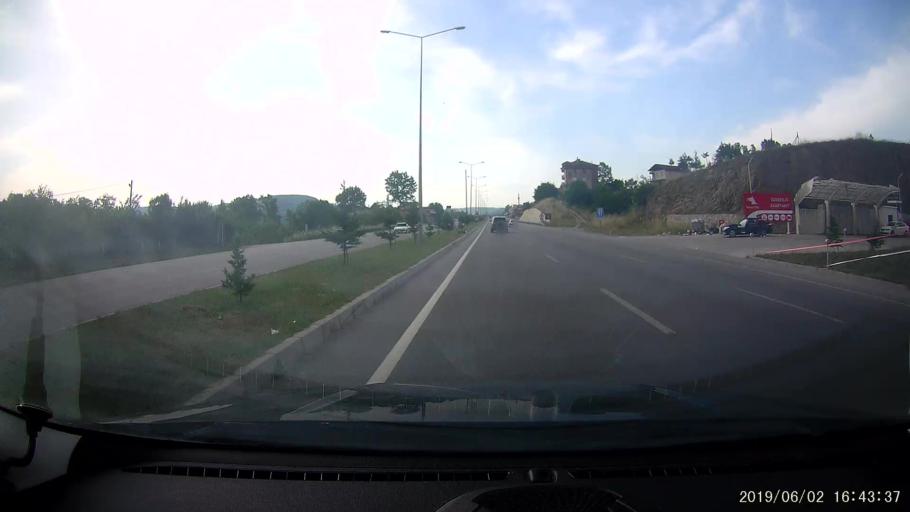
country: TR
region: Samsun
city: Kavak
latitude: 41.1382
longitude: 36.1243
